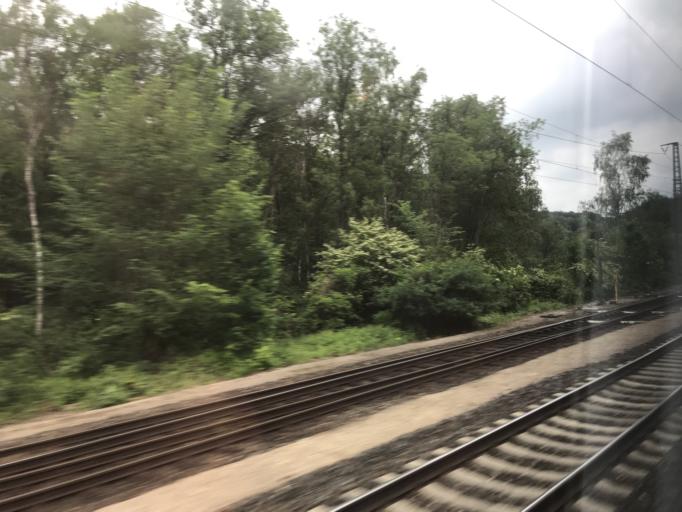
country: DE
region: Bavaria
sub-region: Swabia
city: Offingen
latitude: 48.4796
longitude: 10.3384
